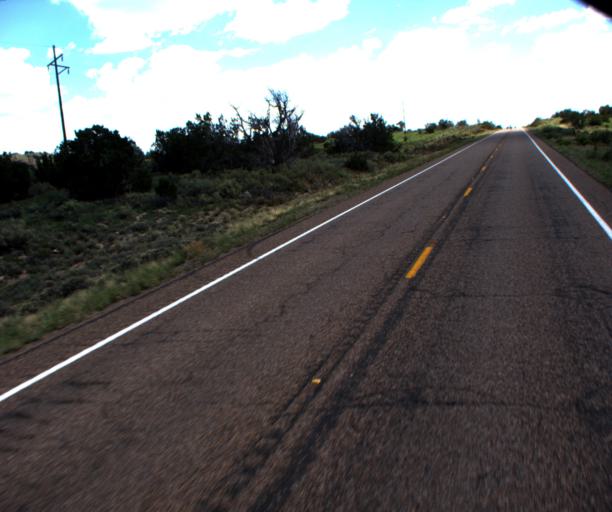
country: US
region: Arizona
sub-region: Coconino County
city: Williams
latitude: 35.5578
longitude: -112.1585
